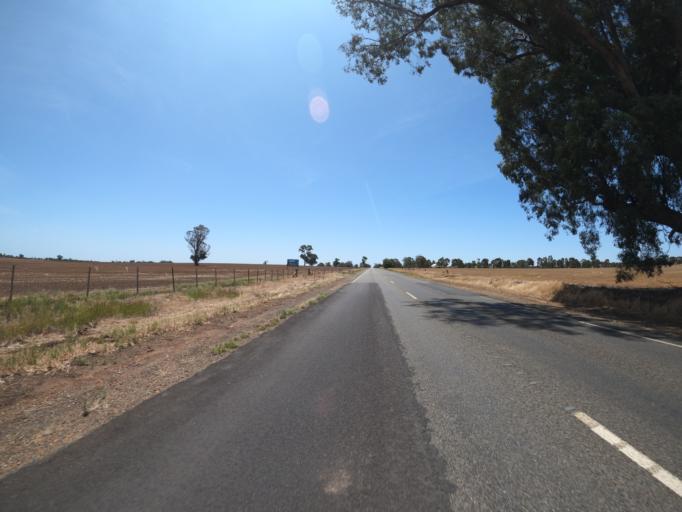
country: AU
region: Victoria
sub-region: Moira
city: Yarrawonga
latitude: -36.0529
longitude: 145.9955
